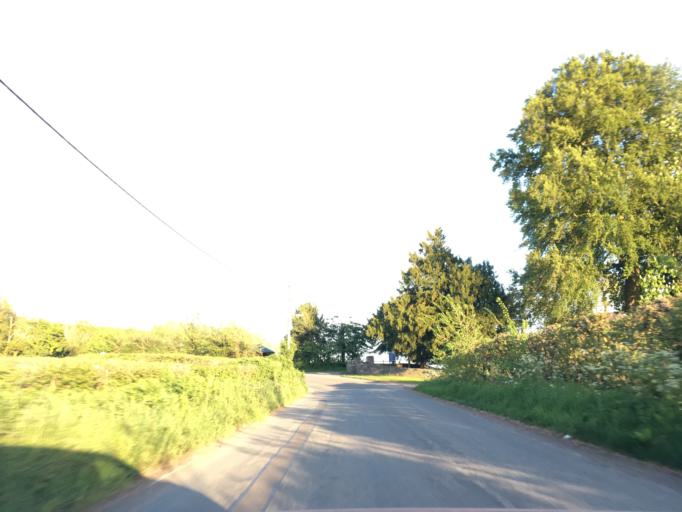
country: GB
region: Wales
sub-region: Newport
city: Llanwern
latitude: 51.5868
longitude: -2.9103
